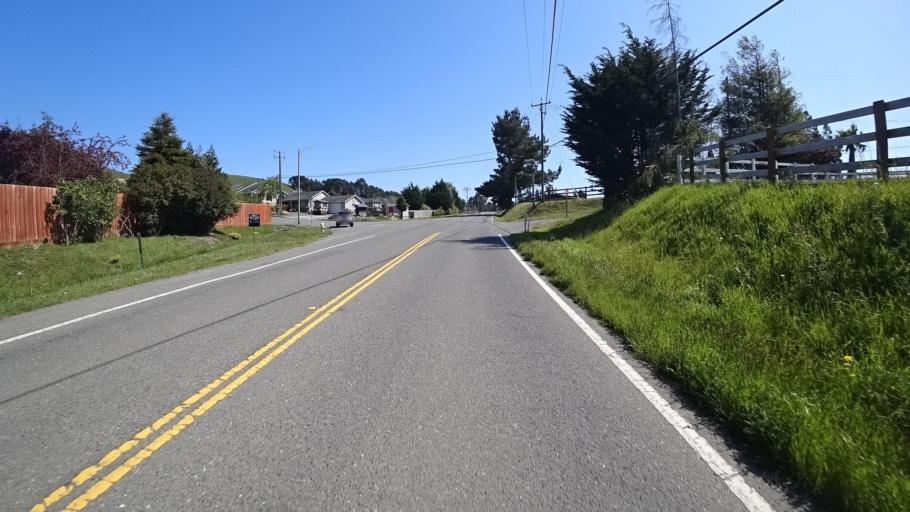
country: US
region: California
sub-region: Humboldt County
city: Hydesville
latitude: 40.5585
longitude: -124.1234
